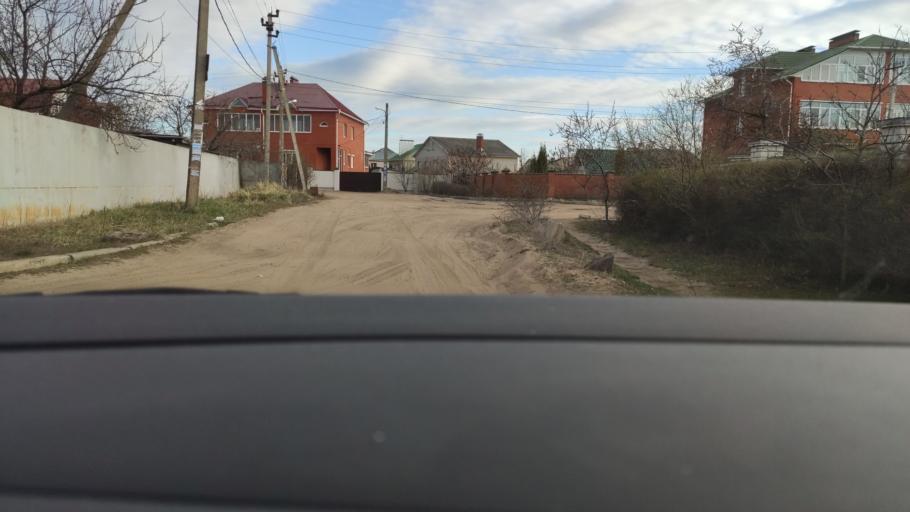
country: RU
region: Voronezj
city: Pridonskoy
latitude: 51.6563
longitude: 39.0917
